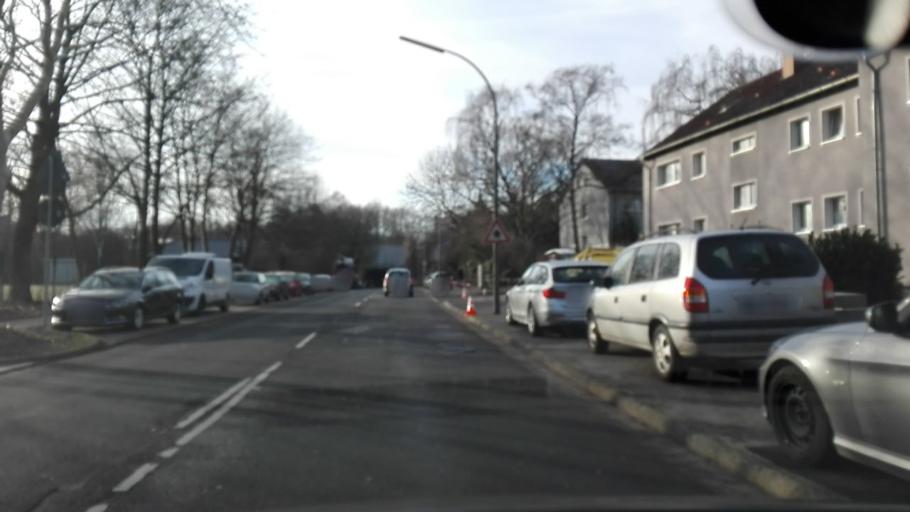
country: DE
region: North Rhine-Westphalia
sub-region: Regierungsbezirk Arnsberg
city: Dortmund
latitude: 51.4984
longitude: 7.4159
